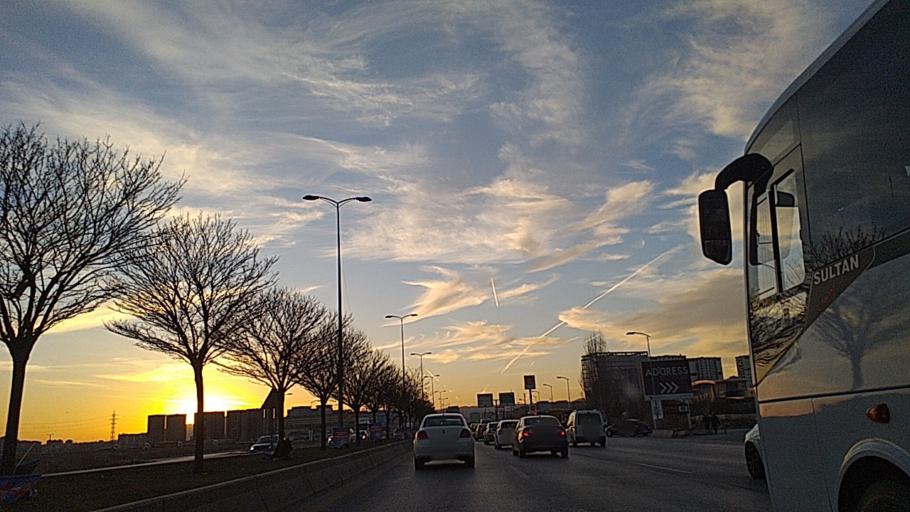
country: TR
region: Ankara
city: Etimesgut
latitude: 39.9647
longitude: 32.6416
